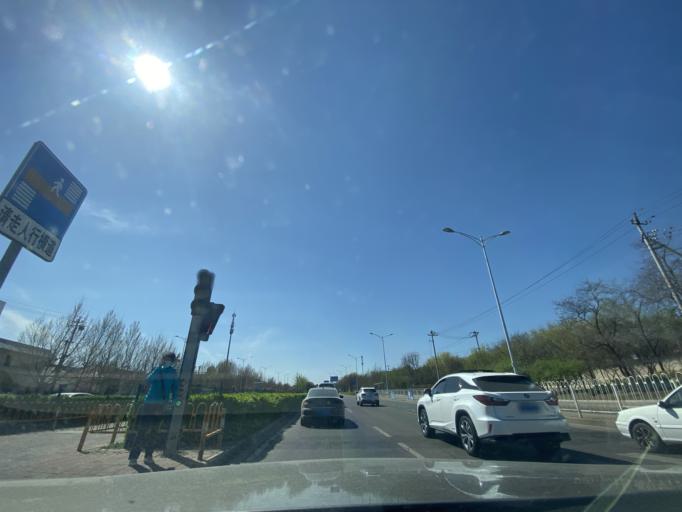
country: CN
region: Beijing
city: Sijiqing
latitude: 39.9421
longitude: 116.2403
